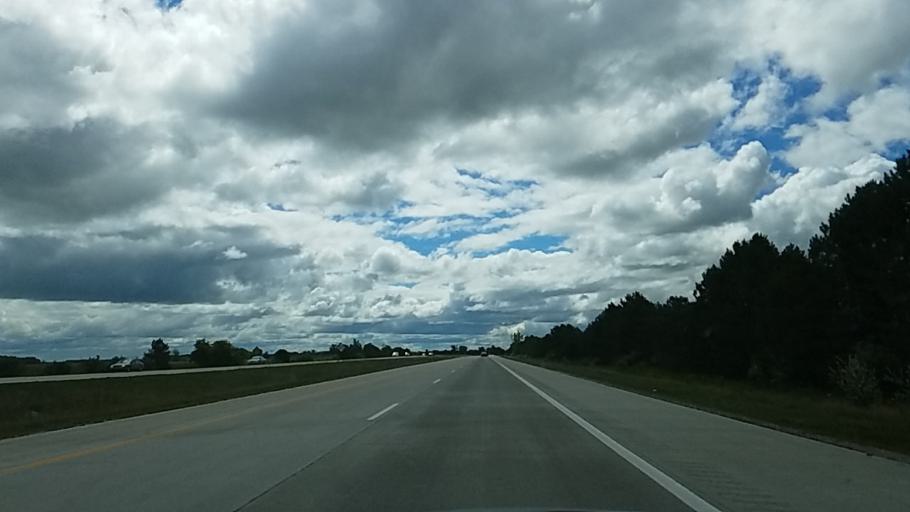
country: US
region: Michigan
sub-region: Bay County
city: Pinconning
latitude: 43.8813
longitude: -84.0215
